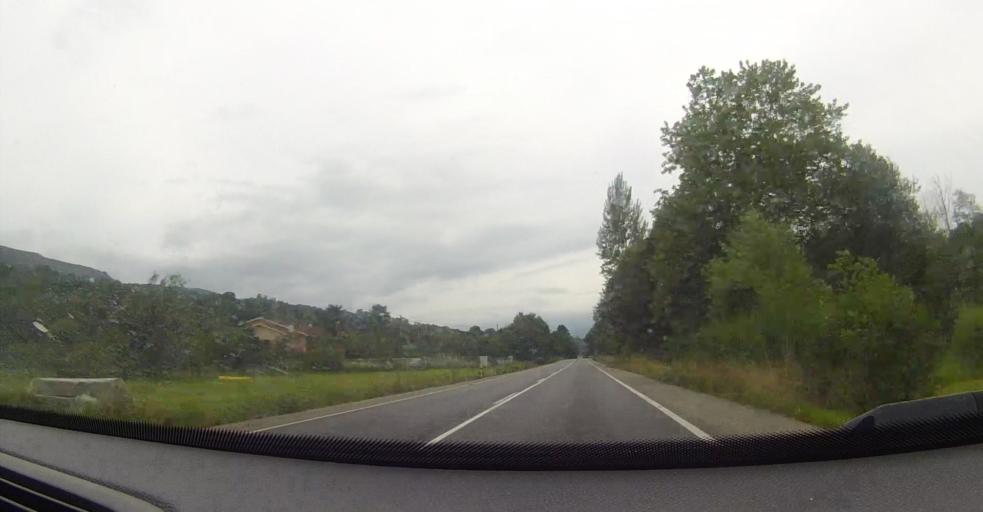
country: ES
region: Asturias
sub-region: Province of Asturias
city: Pilona
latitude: 43.3563
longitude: -5.3137
